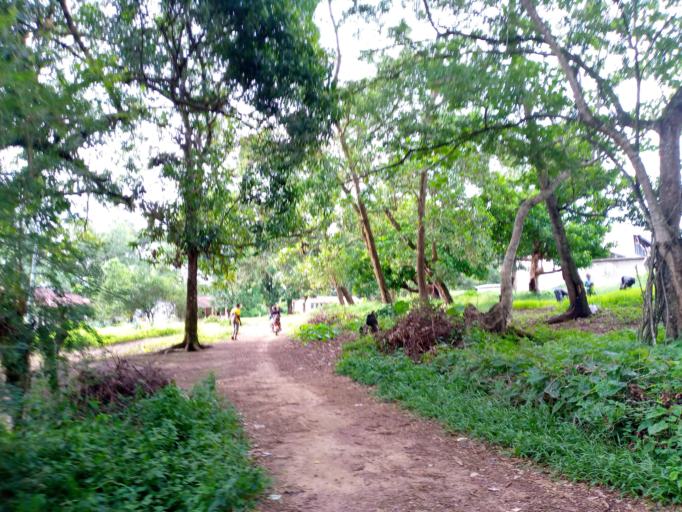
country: SL
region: Northern Province
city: Magburaka
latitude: 8.7182
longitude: -11.9455
